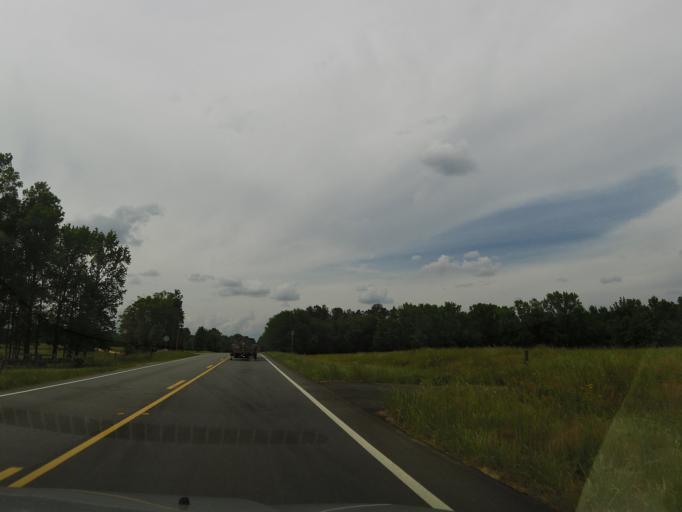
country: US
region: Georgia
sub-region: McDuffie County
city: Thomson
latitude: 33.3809
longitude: -82.4712
